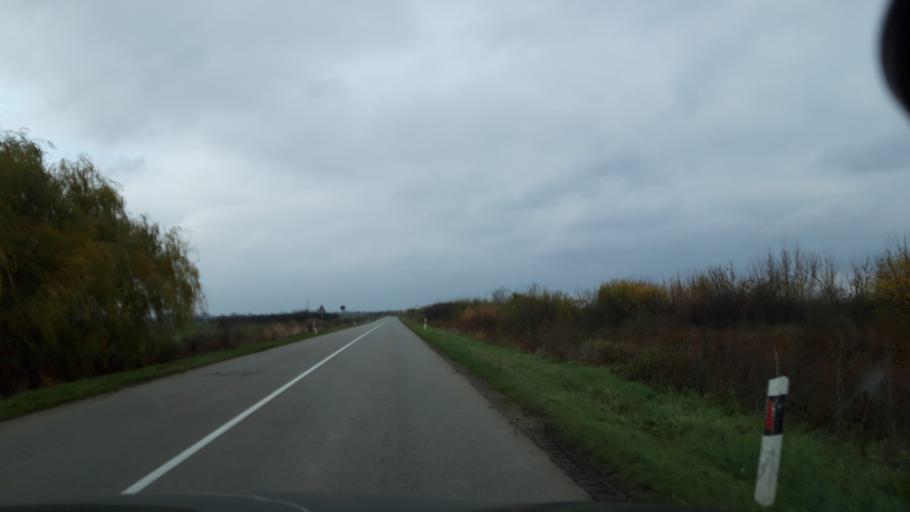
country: RS
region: Autonomna Pokrajina Vojvodina
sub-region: Severnobanatski Okrug
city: Novi Knezevac
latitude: 46.1084
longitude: 20.1027
